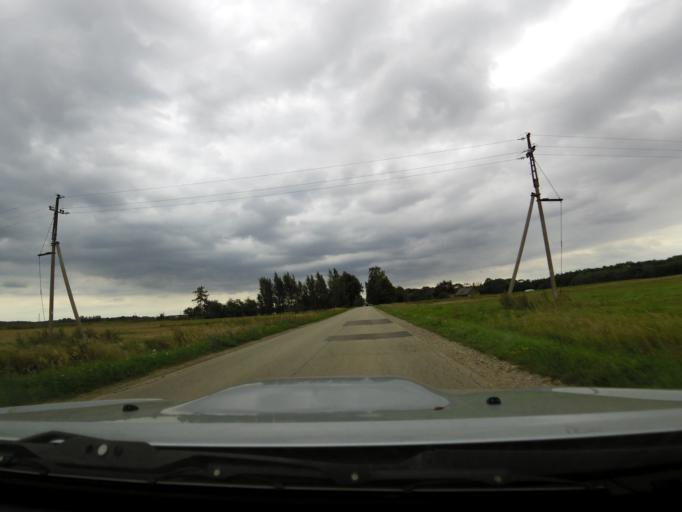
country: LT
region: Panevezys
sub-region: Birzai
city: Birzai
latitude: 56.3209
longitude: 24.8085
